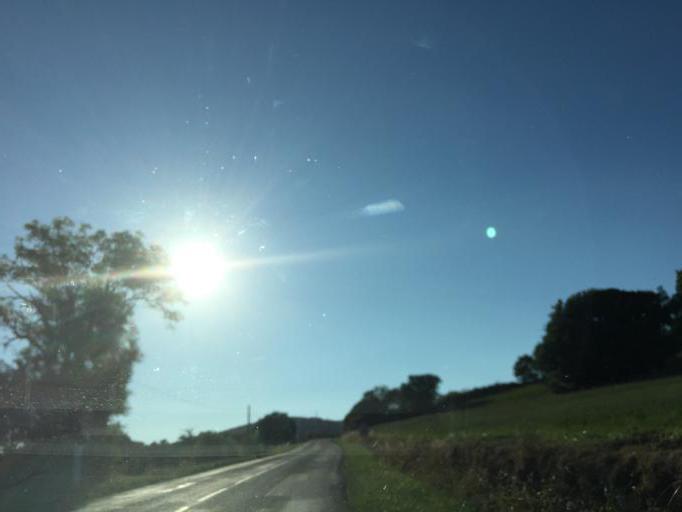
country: FR
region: Midi-Pyrenees
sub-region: Departement de l'Aveyron
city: Saint-Georges-de-Luzencon
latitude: 44.1129
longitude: 2.9017
